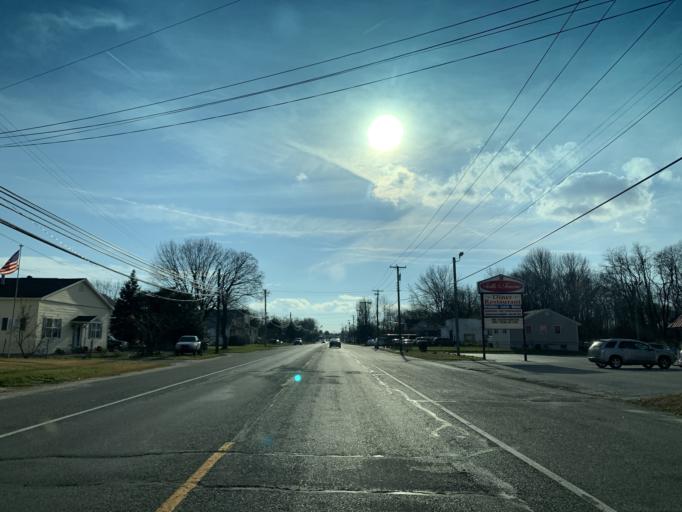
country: US
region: New Jersey
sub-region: Salem County
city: Penns Grove
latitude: 39.7354
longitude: -75.4588
